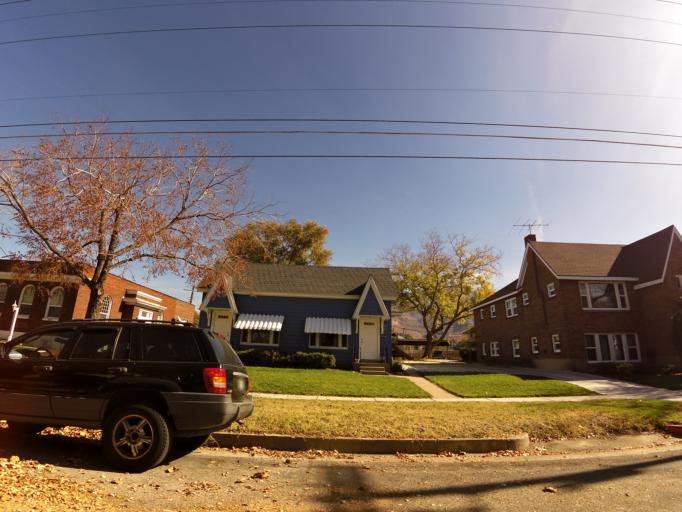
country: US
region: Utah
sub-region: Weber County
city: Ogden
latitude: 41.2240
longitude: -111.9676
